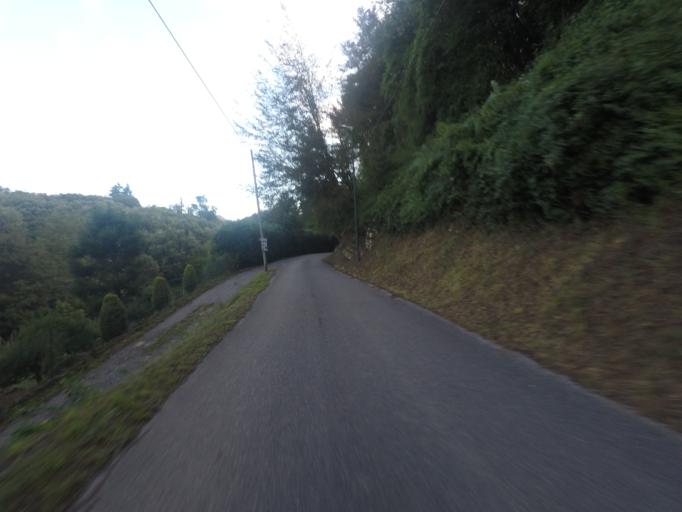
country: IT
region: Tuscany
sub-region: Provincia di Lucca
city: Pescaglia
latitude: 43.9346
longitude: 10.3814
